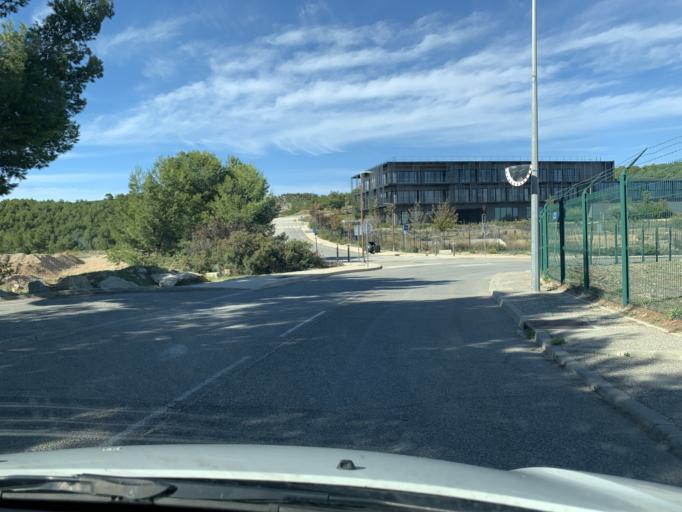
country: FR
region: Provence-Alpes-Cote d'Azur
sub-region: Departement des Bouches-du-Rhone
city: La Ciotat
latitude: 43.2067
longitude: 5.5946
